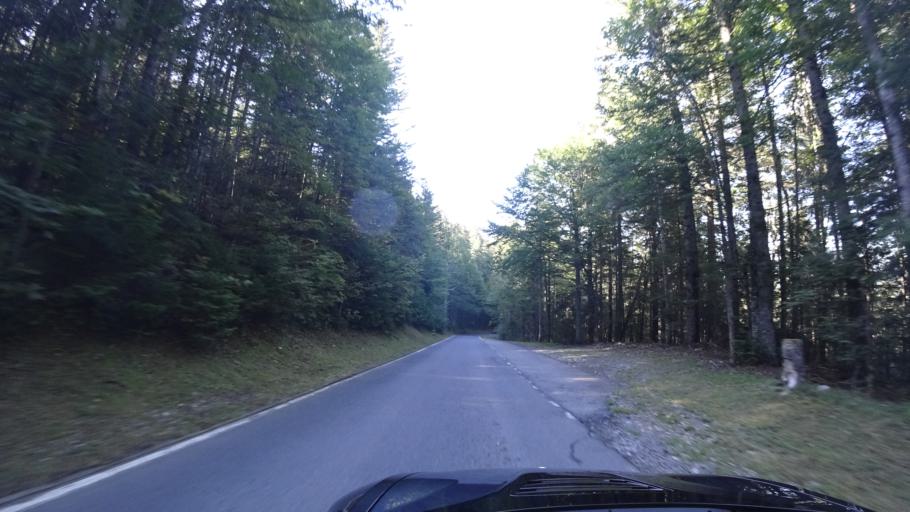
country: CH
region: Obwalden
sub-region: Obwalden
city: Lungern
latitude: 46.8269
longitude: 8.1252
